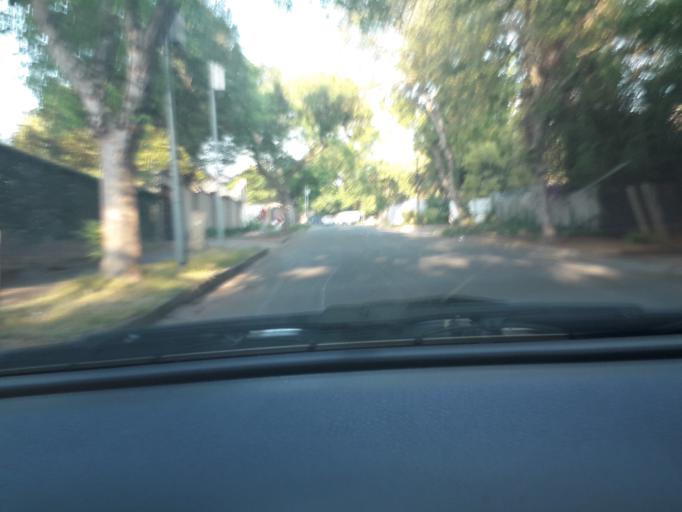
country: ZA
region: Gauteng
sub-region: City of Johannesburg Metropolitan Municipality
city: Johannesburg
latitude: -26.1264
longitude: 28.0758
